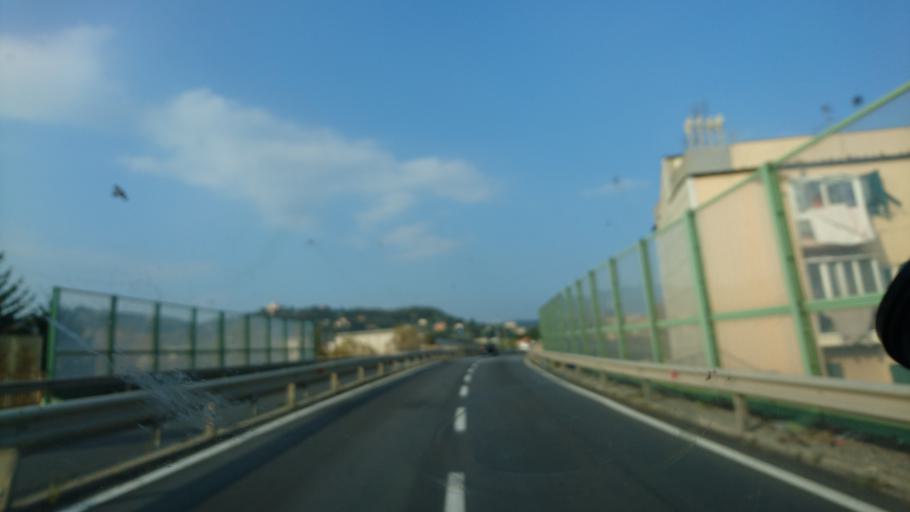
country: IT
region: Liguria
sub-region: Provincia di Savona
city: Valleggia
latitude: 44.2820
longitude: 8.4400
